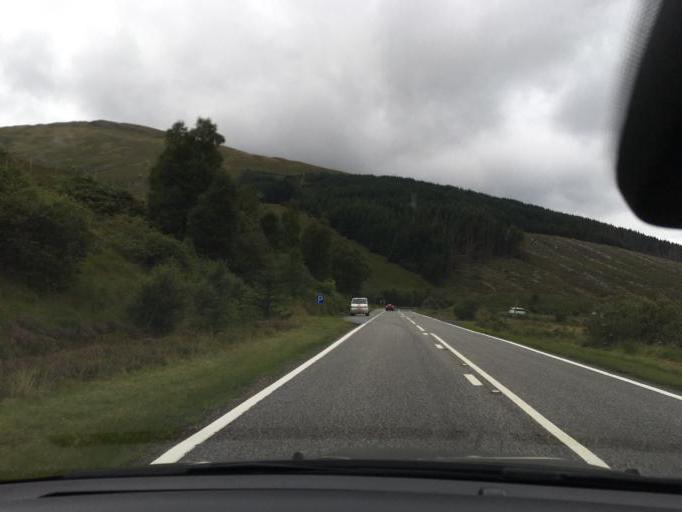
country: GB
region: Scotland
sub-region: Argyll and Bute
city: Garelochhead
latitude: 56.4650
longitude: -4.7215
